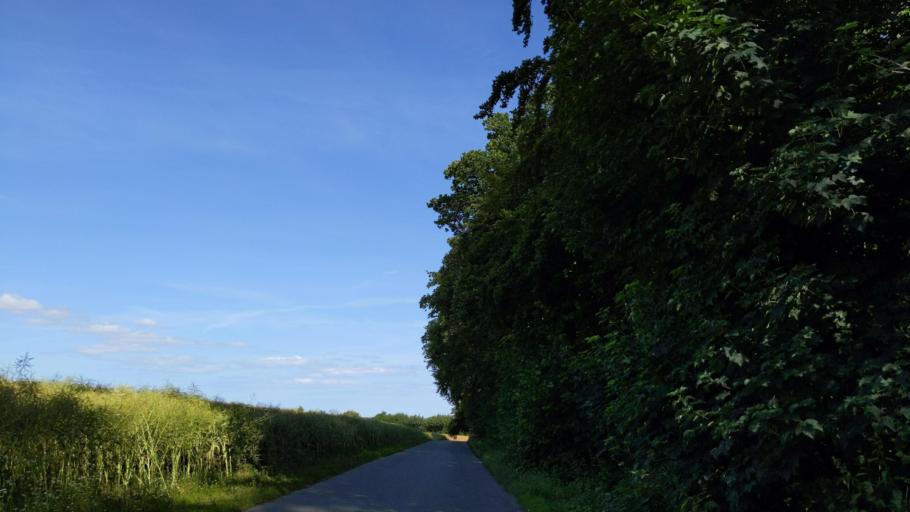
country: DE
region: Schleswig-Holstein
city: Kasseedorf
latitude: 54.1421
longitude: 10.7466
